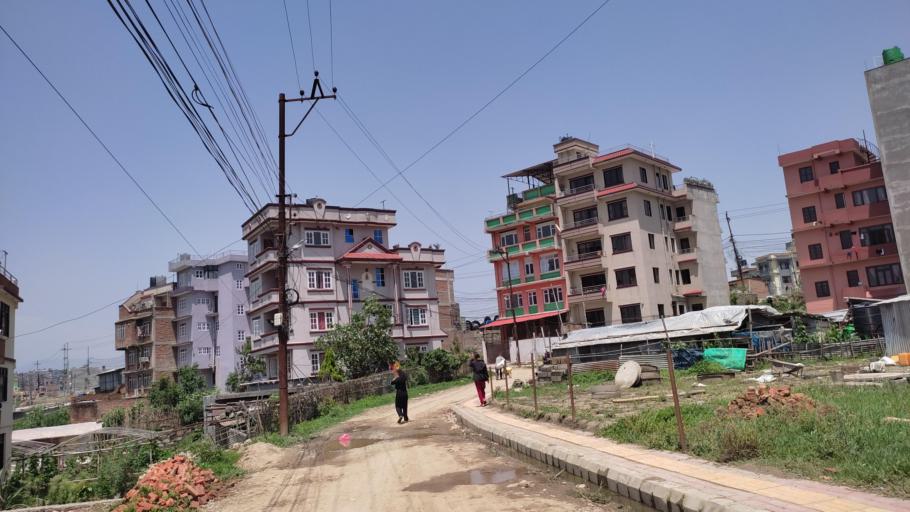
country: NP
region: Central Region
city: Kirtipur
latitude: 27.6712
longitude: 85.2700
